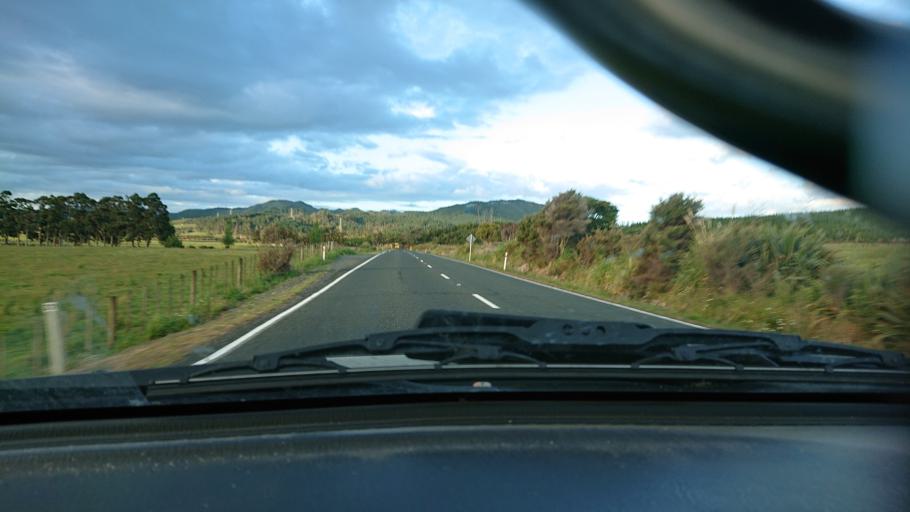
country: NZ
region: Auckland
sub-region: Auckland
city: Parakai
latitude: -36.5175
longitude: 174.4501
